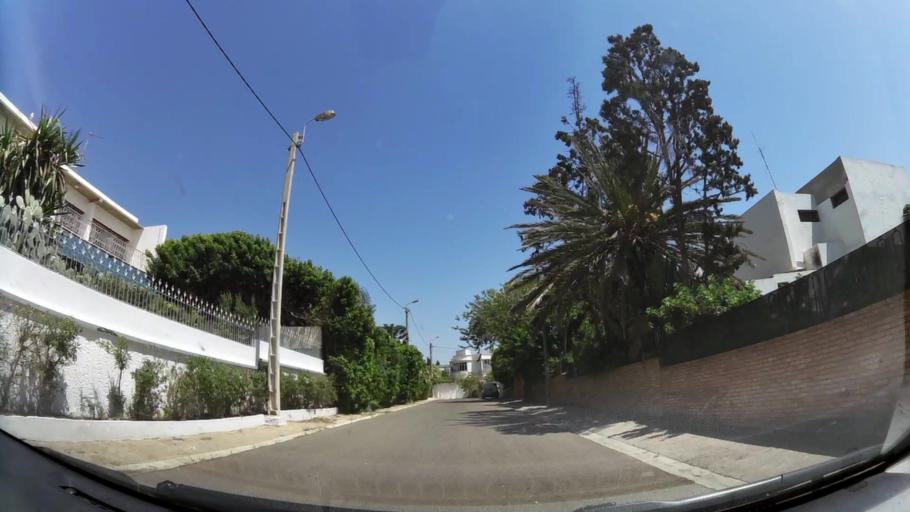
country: MA
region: Souss-Massa-Draa
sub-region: Agadir-Ida-ou-Tnan
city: Agadir
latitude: 30.4286
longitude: -9.5969
